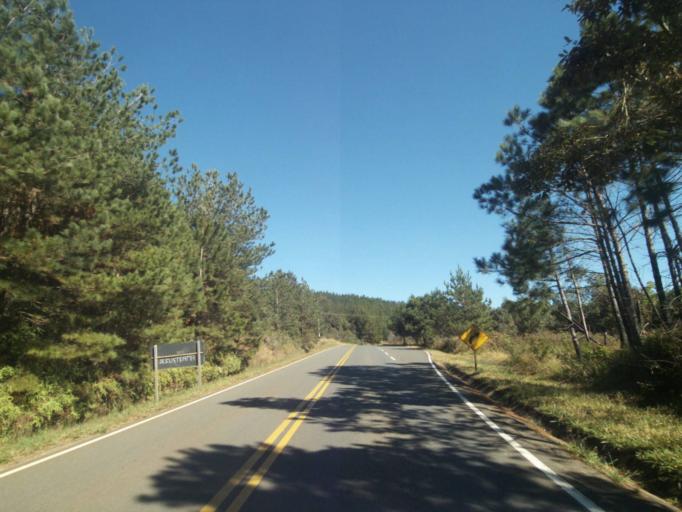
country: BR
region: Parana
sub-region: Telemaco Borba
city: Telemaco Borba
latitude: -24.4231
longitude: -50.5752
